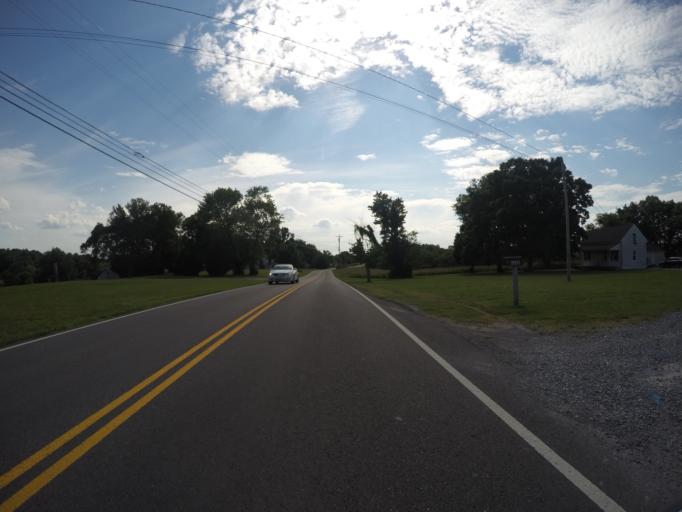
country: US
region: Tennessee
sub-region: Wilson County
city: Mount Juliet
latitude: 36.1691
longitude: -86.5410
